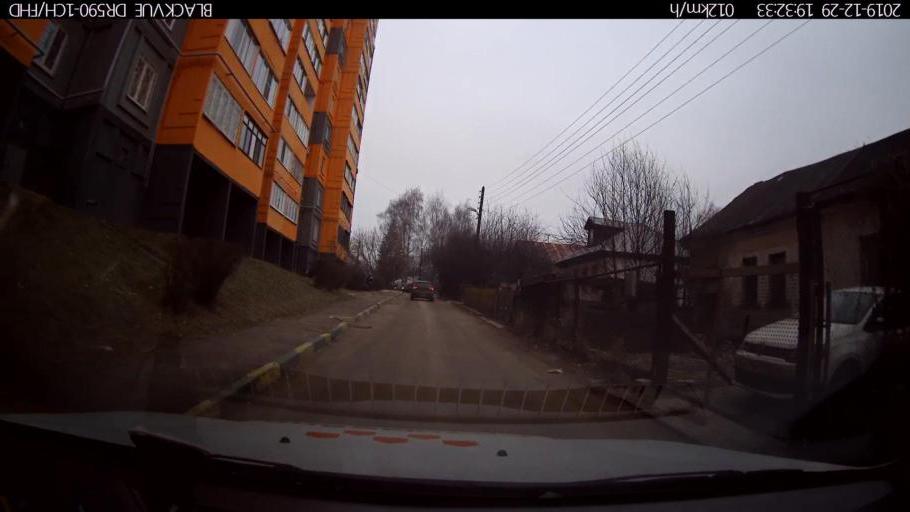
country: RU
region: Nizjnij Novgorod
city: Nizhniy Novgorod
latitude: 56.2985
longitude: 44.0300
